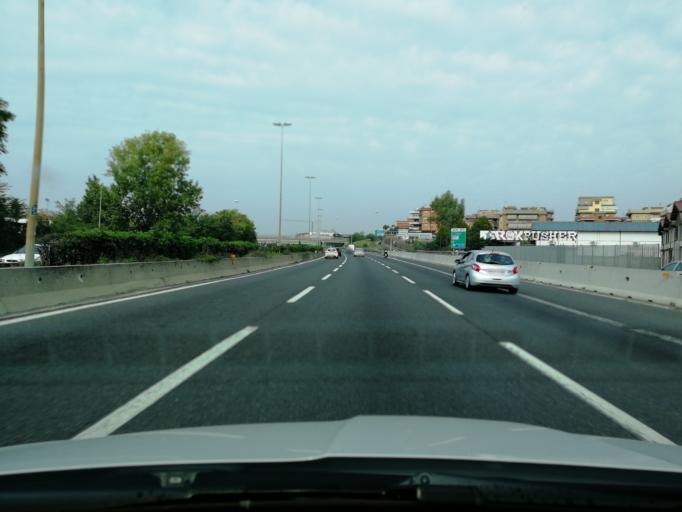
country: IT
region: Latium
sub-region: Citta metropolitana di Roma Capitale
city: Setteville
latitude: 41.8867
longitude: 12.6136
